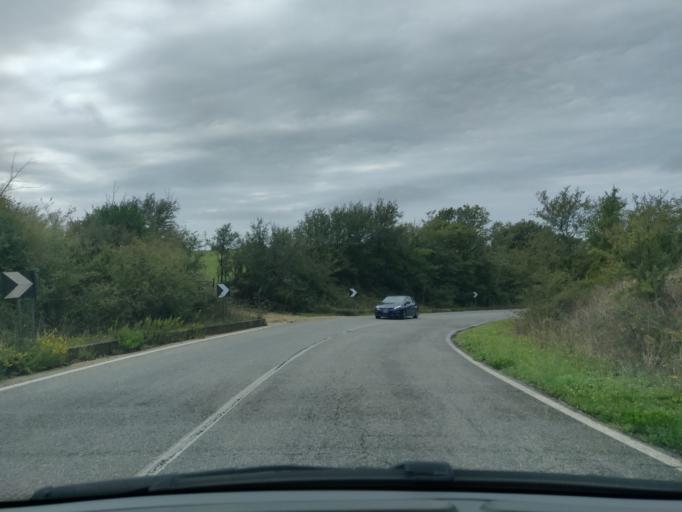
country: IT
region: Latium
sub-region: Citta metropolitana di Roma Capitale
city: Allumiere
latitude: 42.1144
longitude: 11.8571
